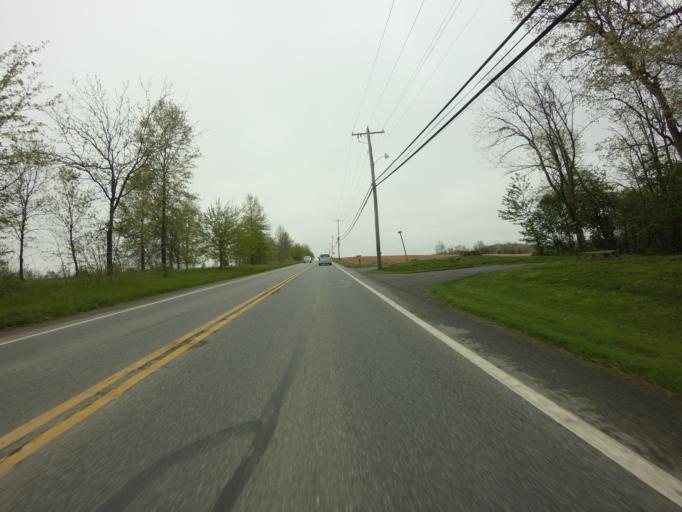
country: US
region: Maryland
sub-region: Carroll County
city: New Windsor
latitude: 39.5127
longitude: -77.1167
